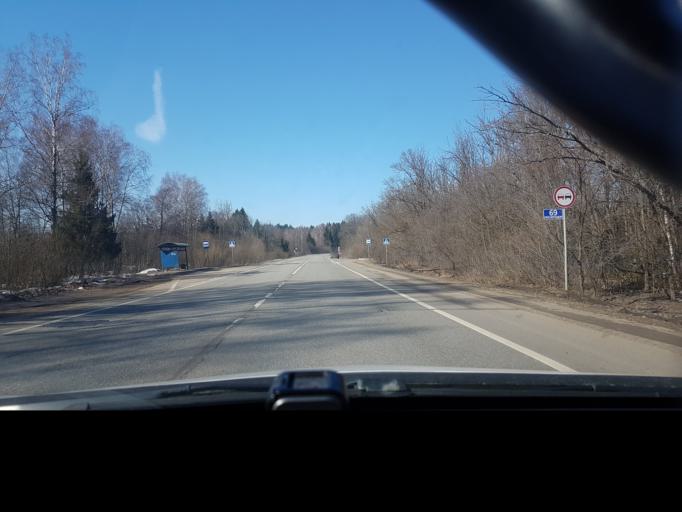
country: RU
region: Moskovskaya
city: Kostrovo
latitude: 55.9185
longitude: 36.6706
